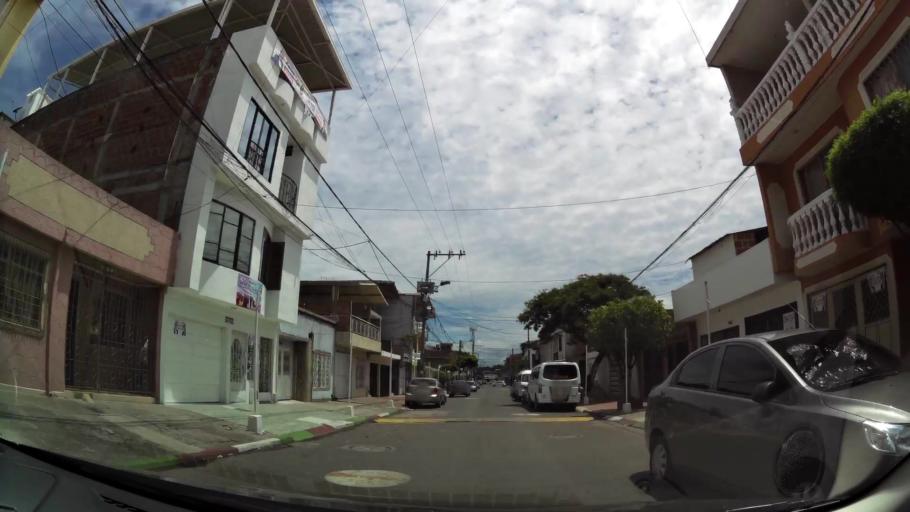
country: CO
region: Valle del Cauca
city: Cali
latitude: 3.4388
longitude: -76.5097
